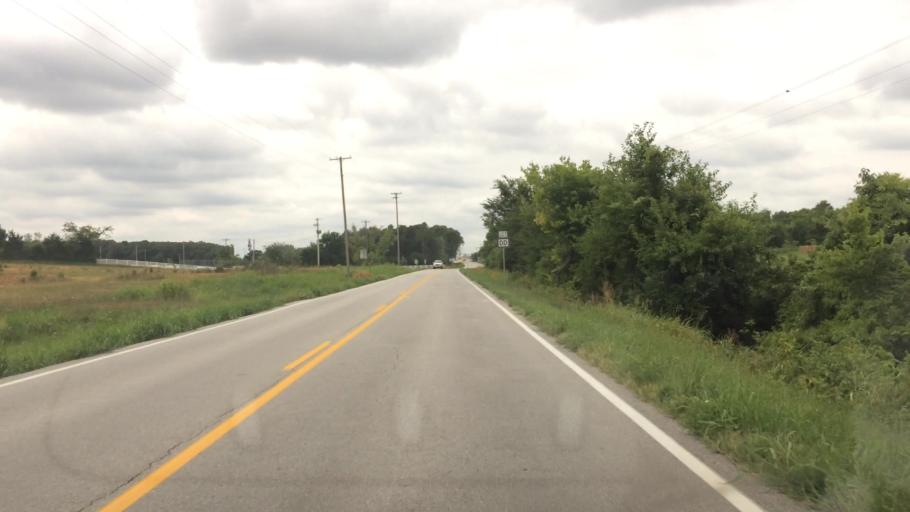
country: US
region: Missouri
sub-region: Greene County
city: Strafford
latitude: 37.2832
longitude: -93.1131
